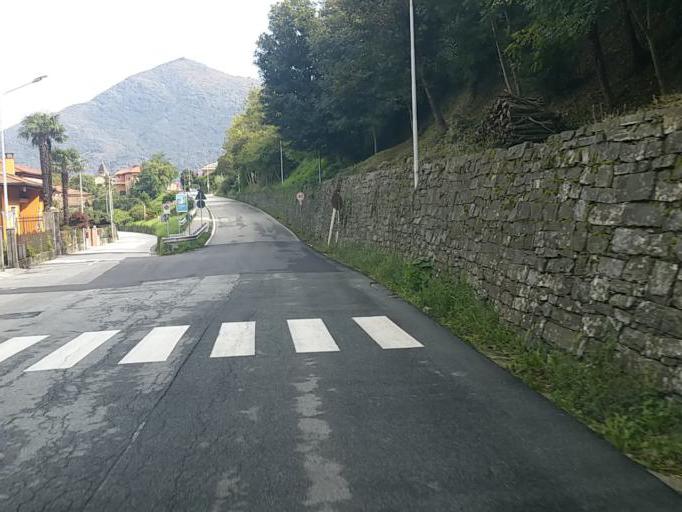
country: IT
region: Piedmont
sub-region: Provincia Verbano-Cusio-Ossola
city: Cannobio
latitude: 46.0583
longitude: 8.6902
